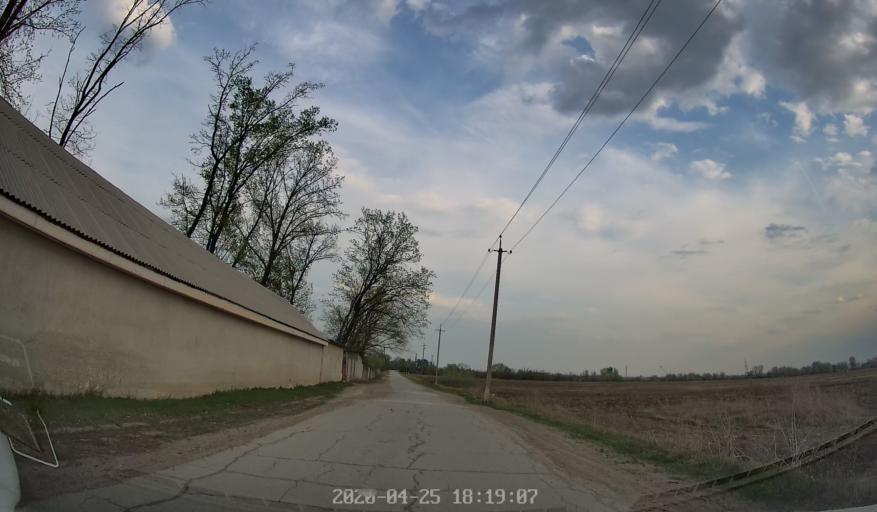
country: MD
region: Criuleni
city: Criuleni
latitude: 47.1609
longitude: 29.1295
